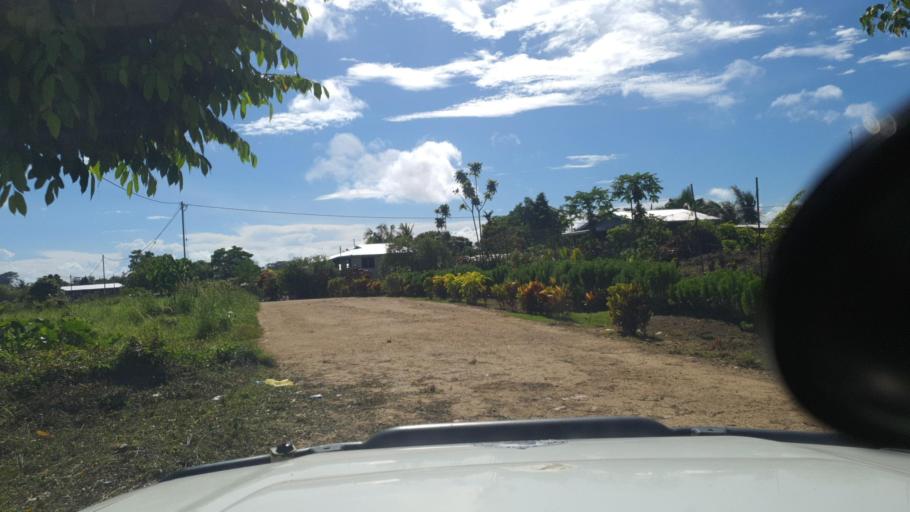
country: SB
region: Western Province
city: Gizo
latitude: -8.2429
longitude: 157.1989
